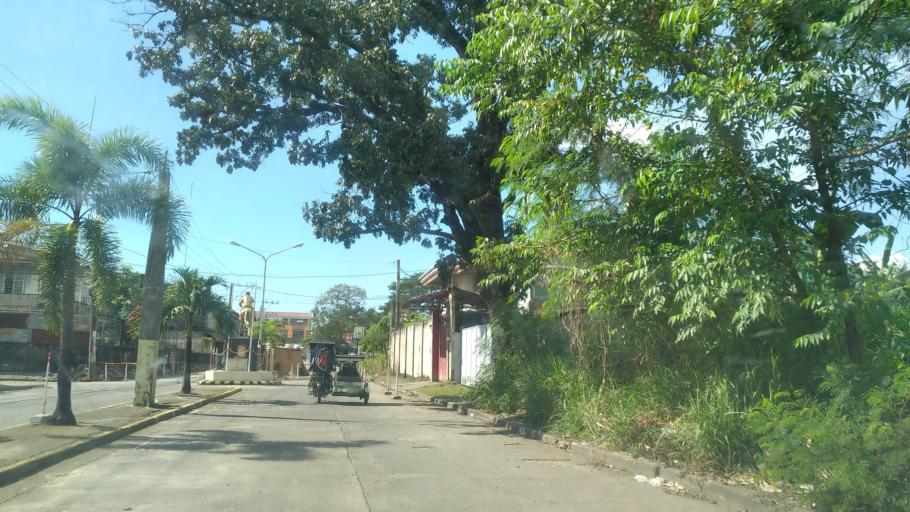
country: PH
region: Calabarzon
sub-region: Province of Quezon
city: Lucena
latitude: 13.9380
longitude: 121.6008
